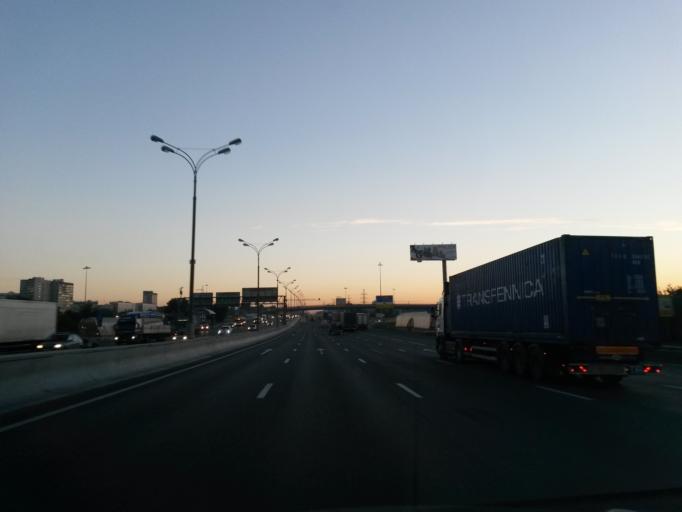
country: RU
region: Moscow
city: Ivanovskoye
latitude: 55.7731
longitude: 37.8432
